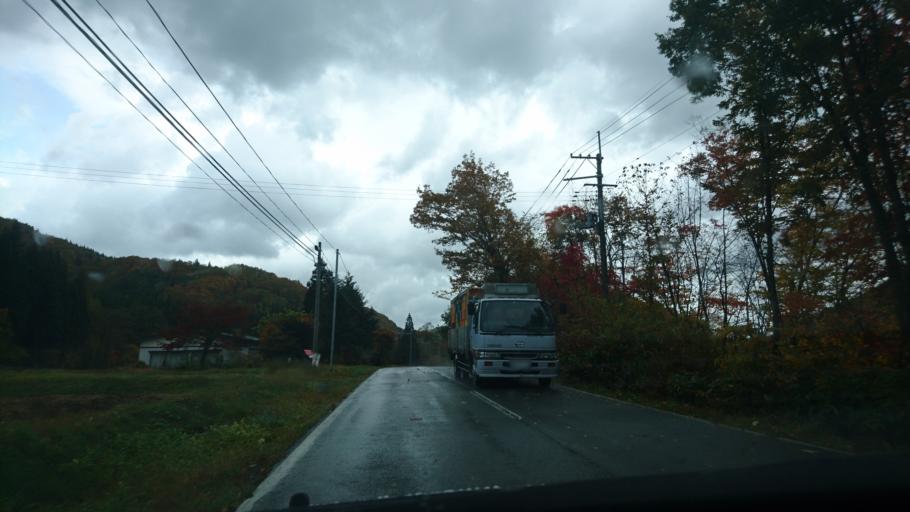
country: JP
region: Iwate
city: Shizukuishi
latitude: 39.6133
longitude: 140.9440
